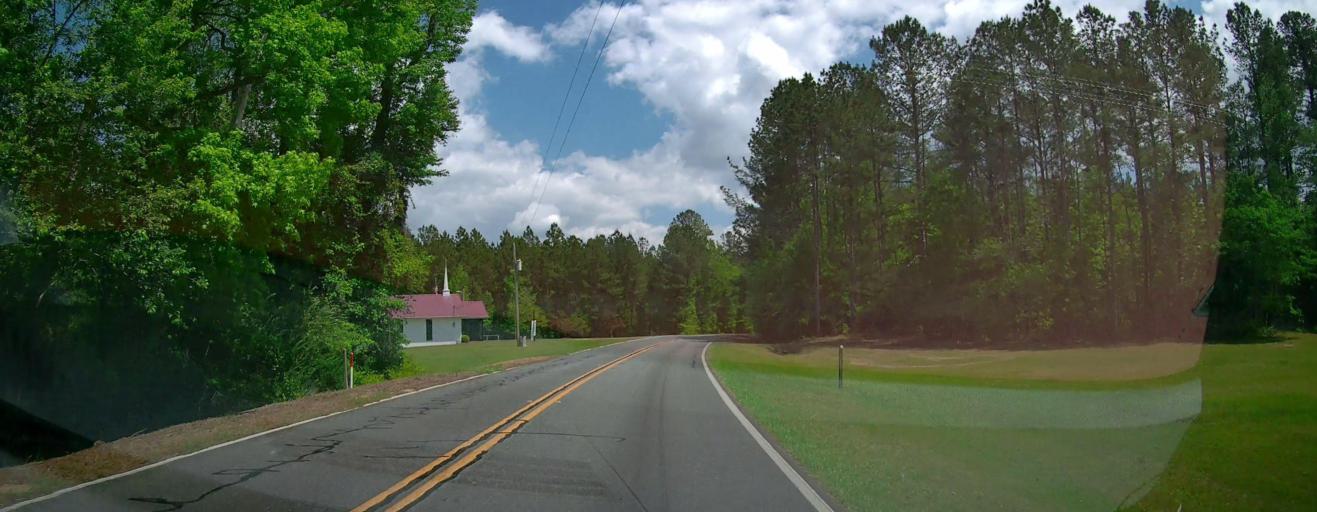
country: US
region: Georgia
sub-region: Treutlen County
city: Soperton
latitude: 32.5068
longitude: -82.6247
